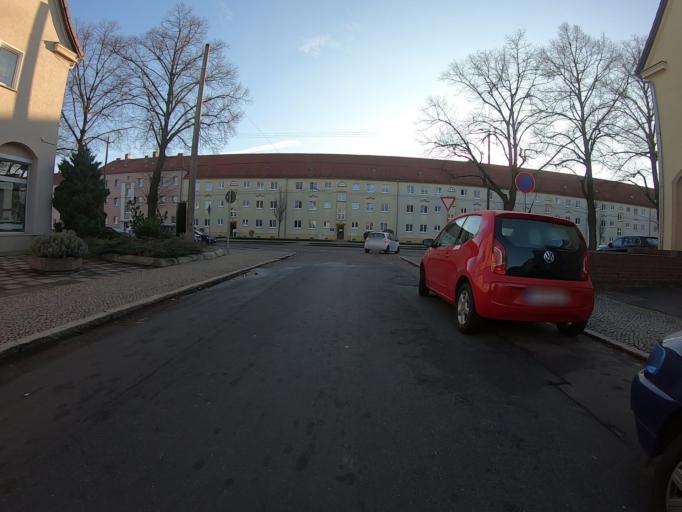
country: DE
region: Saxony-Anhalt
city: Halle (Saale)
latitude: 51.5078
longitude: 11.9922
